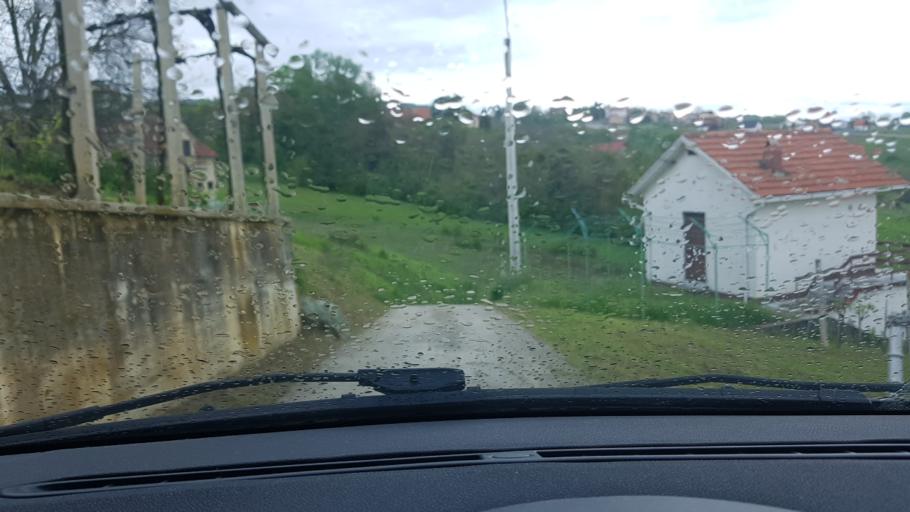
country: HR
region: Krapinsko-Zagorska
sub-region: Grad Krapina
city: Krapina
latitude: 46.1688
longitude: 15.8166
